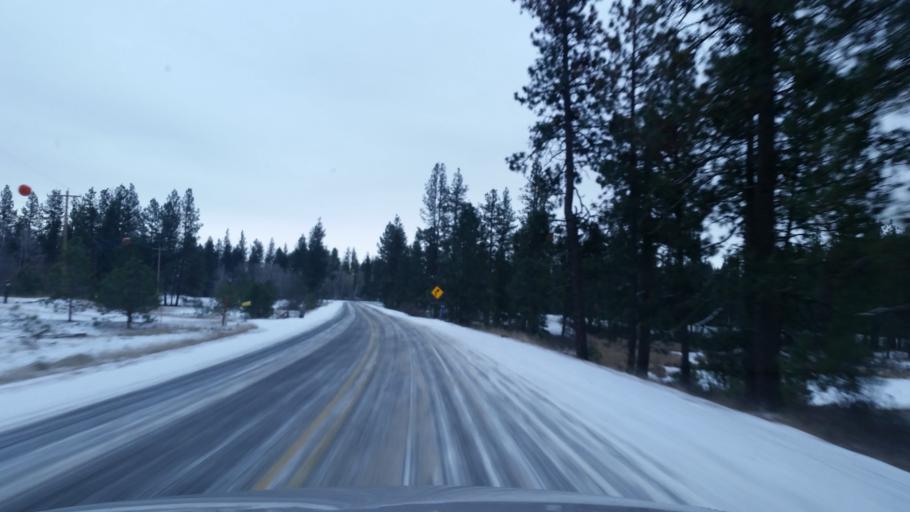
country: US
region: Washington
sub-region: Spokane County
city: Cheney
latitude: 47.4549
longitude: -117.5245
